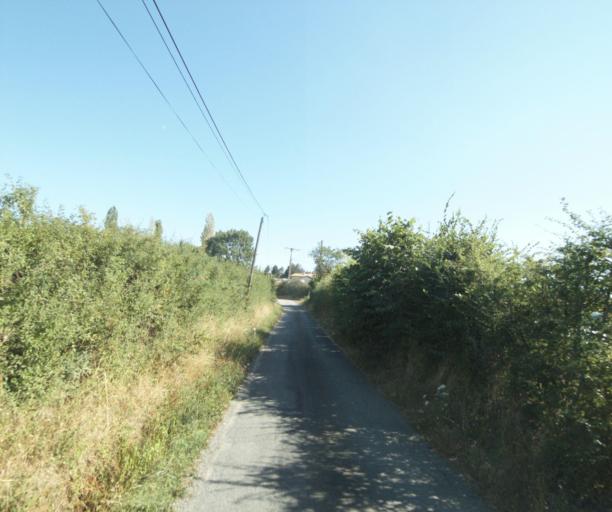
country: FR
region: Rhone-Alpes
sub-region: Departement du Rhone
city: La Tour-de-Salvagny
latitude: 45.8292
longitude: 4.7237
